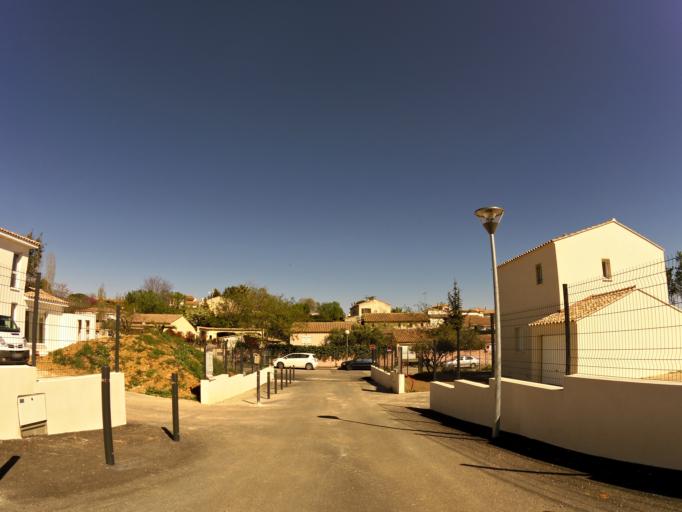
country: FR
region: Languedoc-Roussillon
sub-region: Departement du Gard
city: Mus
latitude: 43.7385
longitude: 4.2024
